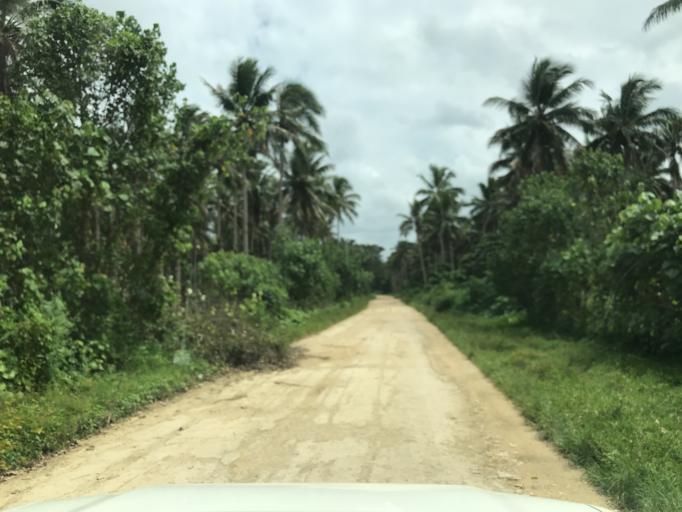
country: VU
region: Sanma
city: Port-Olry
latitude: -15.1767
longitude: 167.0956
